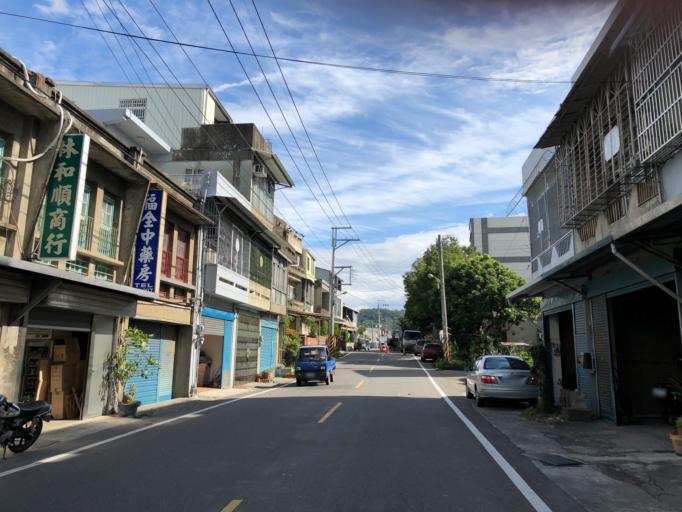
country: TW
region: Taiwan
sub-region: Hsinchu
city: Zhubei
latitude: 24.7910
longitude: 121.0631
